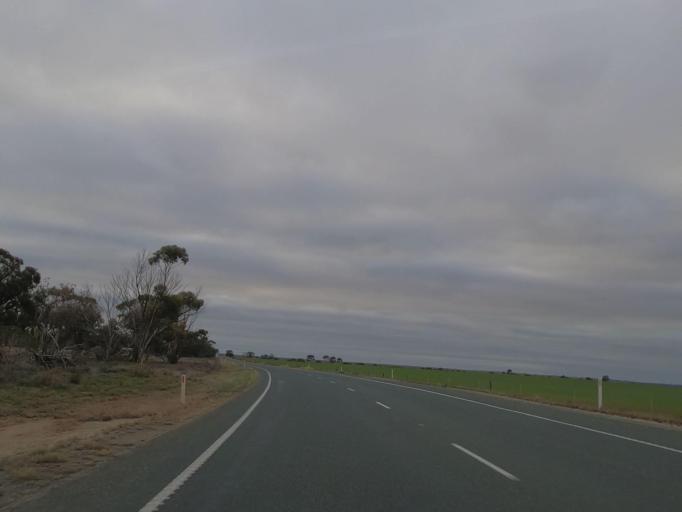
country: AU
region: Victoria
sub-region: Swan Hill
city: Swan Hill
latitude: -35.5626
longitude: 143.7825
